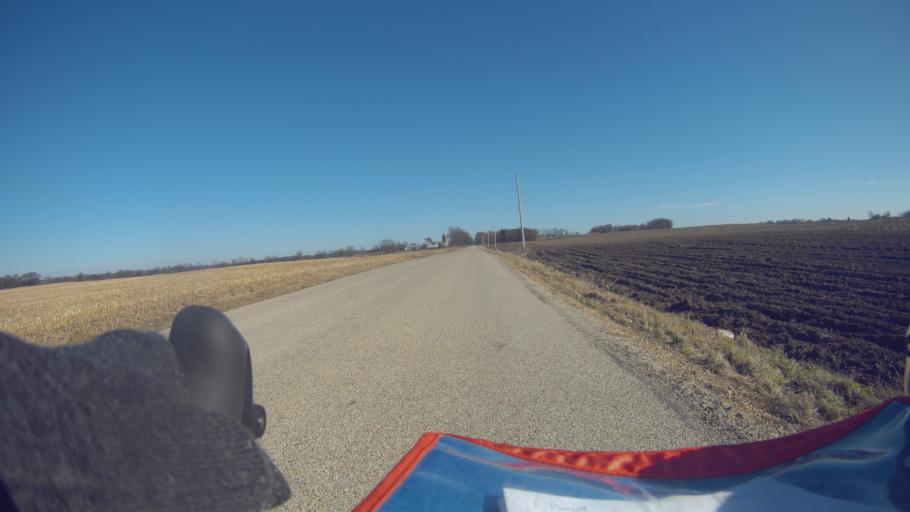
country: US
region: Wisconsin
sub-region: Green County
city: Brooklyn
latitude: 42.8382
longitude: -89.3220
